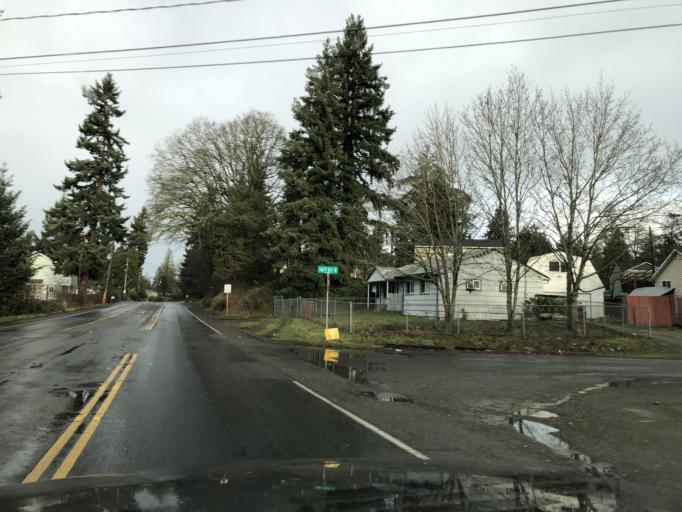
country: US
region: Washington
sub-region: Pierce County
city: Parkland
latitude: 47.1599
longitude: -122.4391
